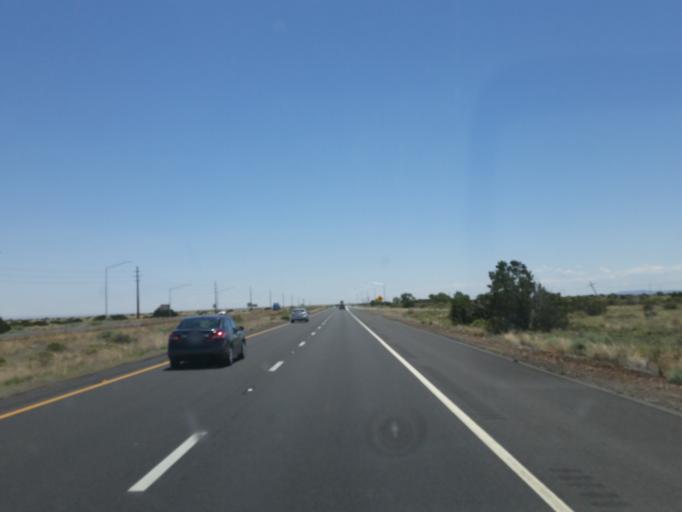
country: US
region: Arizona
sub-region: Coconino County
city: Flagstaff
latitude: 35.1608
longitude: -111.2707
